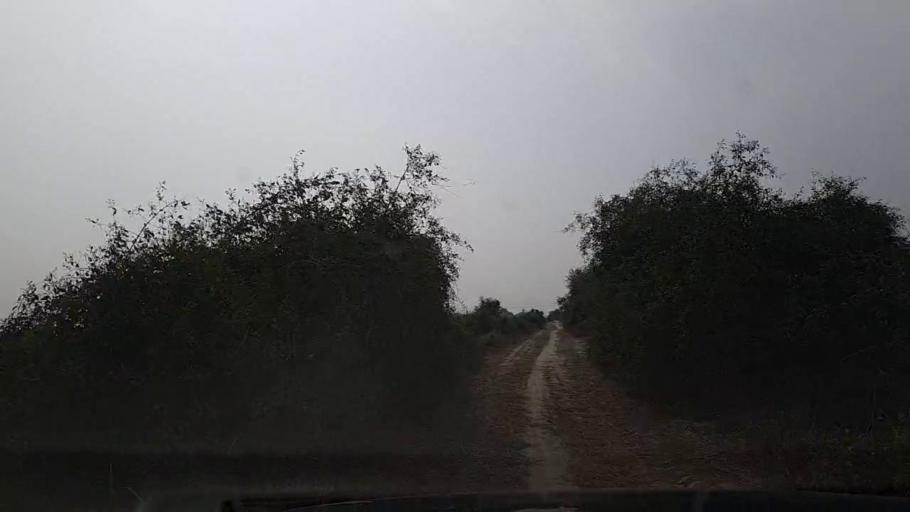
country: PK
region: Sindh
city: Thatta
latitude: 24.7462
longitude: 67.8068
